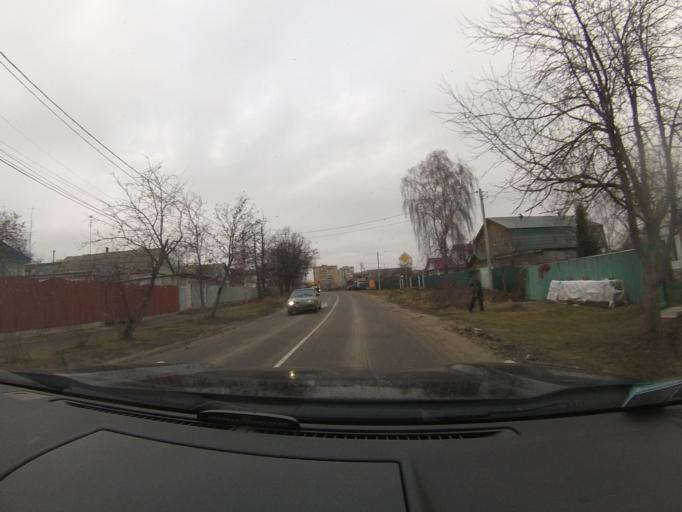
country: RU
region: Moskovskaya
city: Peski
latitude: 55.2667
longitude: 38.7548
